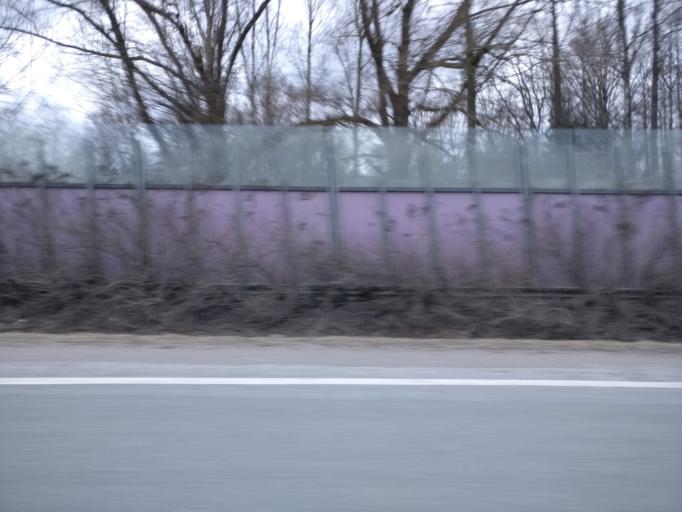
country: FI
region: Haeme
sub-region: Haemeenlinna
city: Haemeenlinna
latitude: 60.9889
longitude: 24.4598
